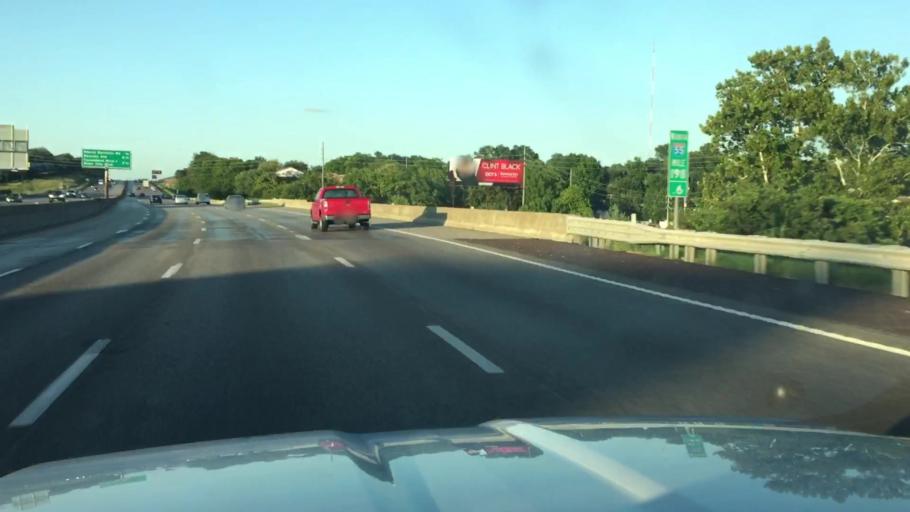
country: US
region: Missouri
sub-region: Saint Louis County
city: Mehlville
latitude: 38.5231
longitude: -90.3212
